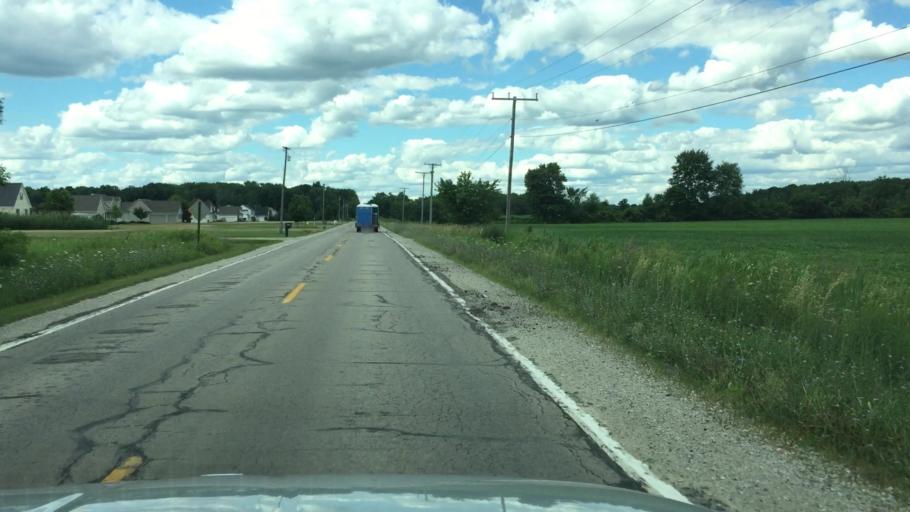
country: US
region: Michigan
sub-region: Saint Clair County
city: Capac
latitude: 42.9322
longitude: -82.9458
